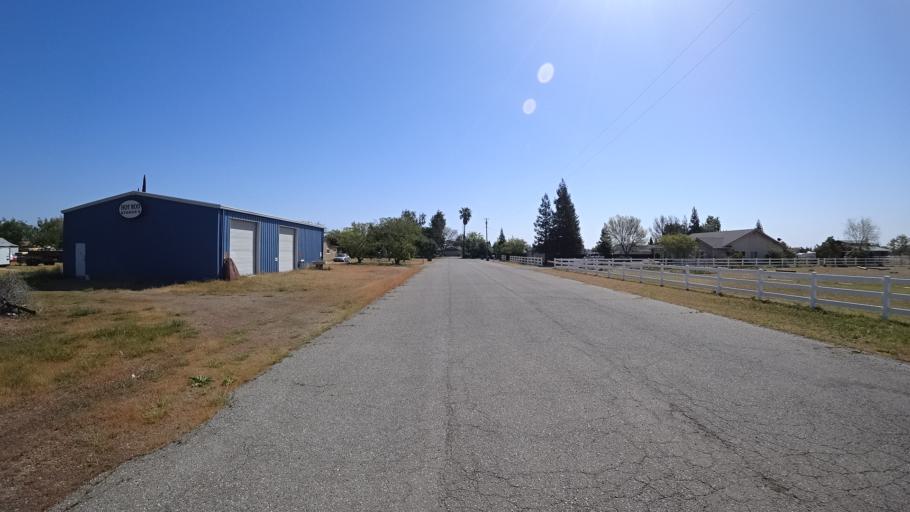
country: US
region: California
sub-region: Glenn County
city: Orland
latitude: 39.7294
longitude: -122.1921
